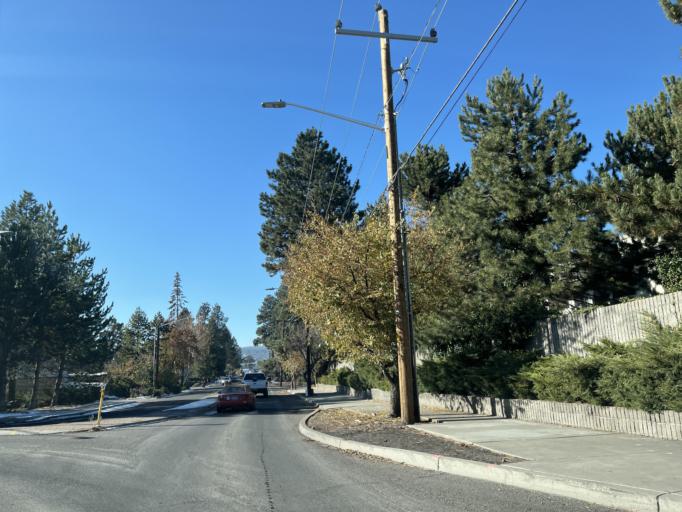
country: US
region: Oregon
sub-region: Deschutes County
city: Bend
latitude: 44.0763
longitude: -121.2902
